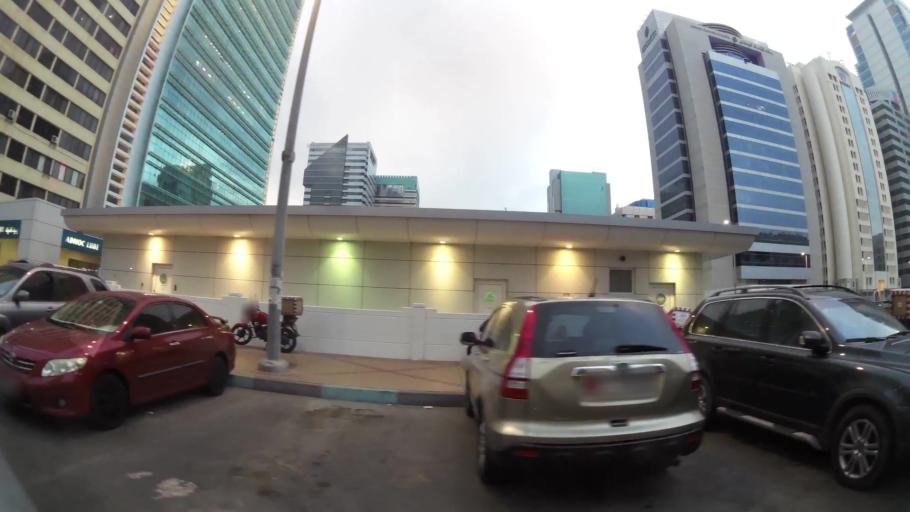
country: AE
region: Abu Dhabi
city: Abu Dhabi
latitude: 24.4921
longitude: 54.3745
